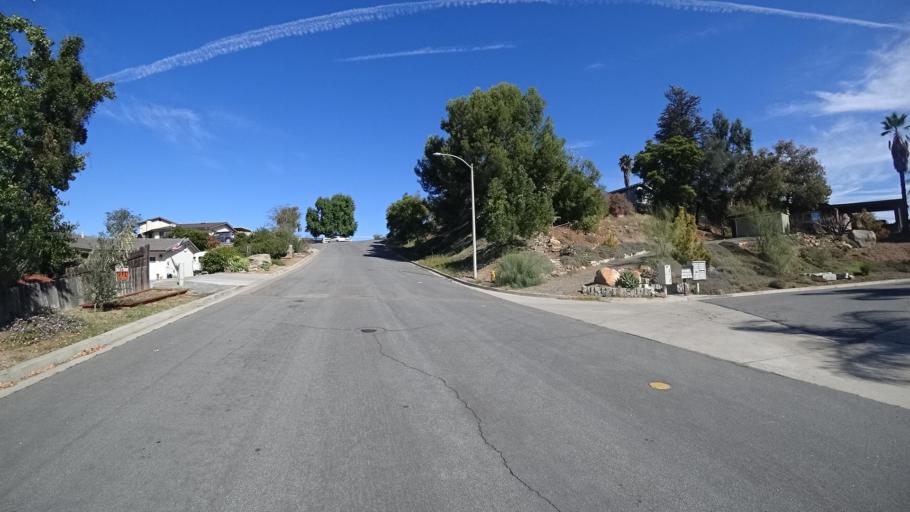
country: US
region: California
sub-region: San Diego County
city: Lakeside
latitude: 32.8436
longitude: -116.8945
